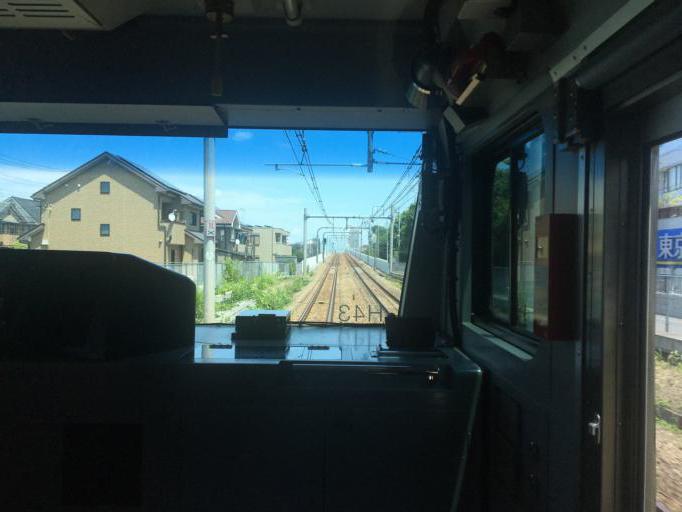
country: JP
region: Tokyo
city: Kokubunji
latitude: 35.7006
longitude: 139.4891
